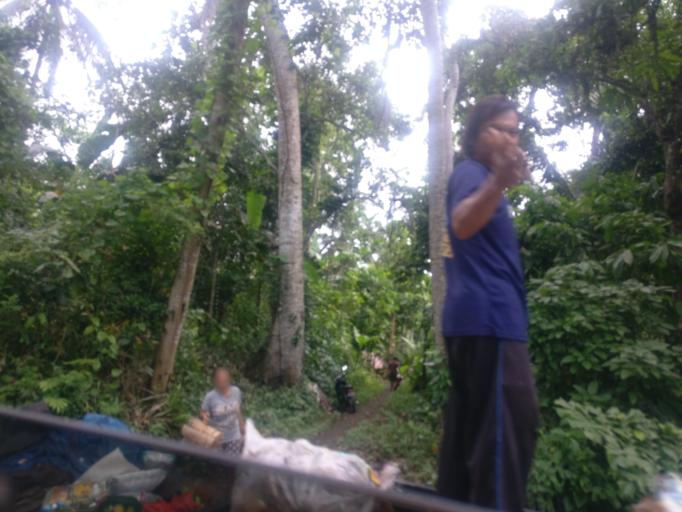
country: ID
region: Bali
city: Banjar Kawan
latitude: -8.4892
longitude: 115.5161
